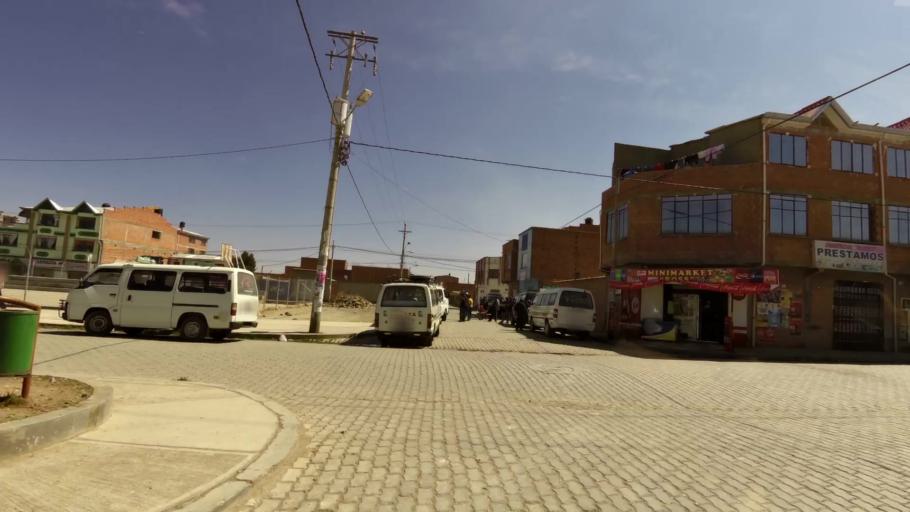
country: BO
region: La Paz
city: La Paz
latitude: -16.5361
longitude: -68.1540
